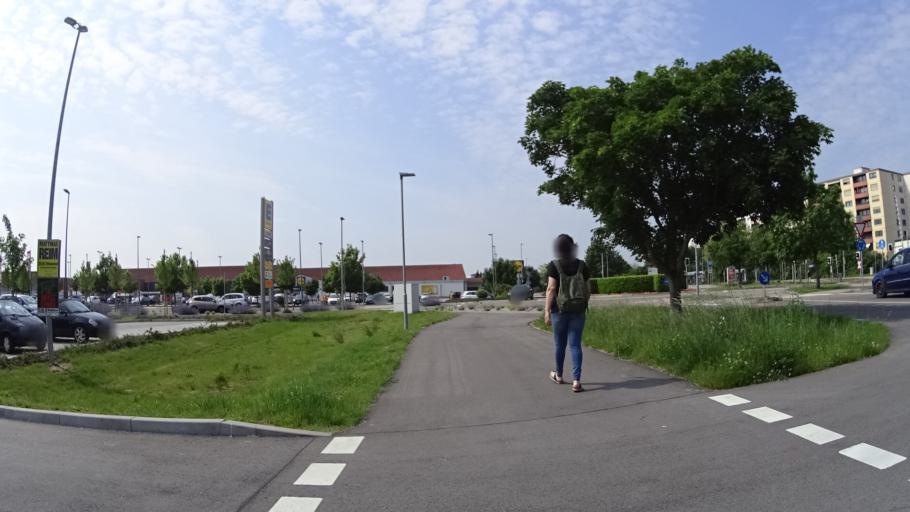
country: DE
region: Baden-Wuerttemberg
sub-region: Karlsruhe Region
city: Linkenheim-Hochstetten
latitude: 49.1302
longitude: 8.4170
